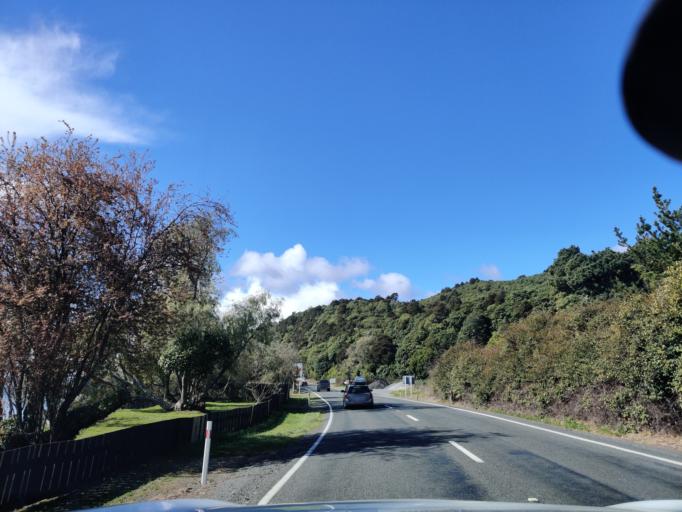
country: NZ
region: Waikato
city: Turangi
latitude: -38.8863
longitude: 175.9630
